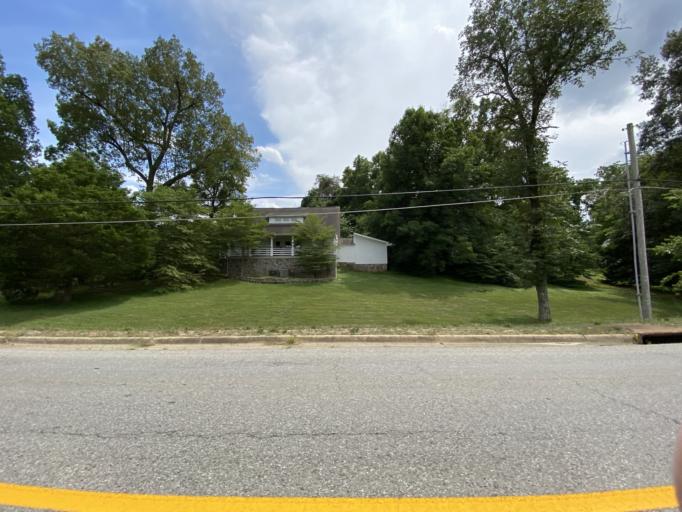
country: US
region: Missouri
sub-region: Oregon County
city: Thayer
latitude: 36.4957
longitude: -91.5448
